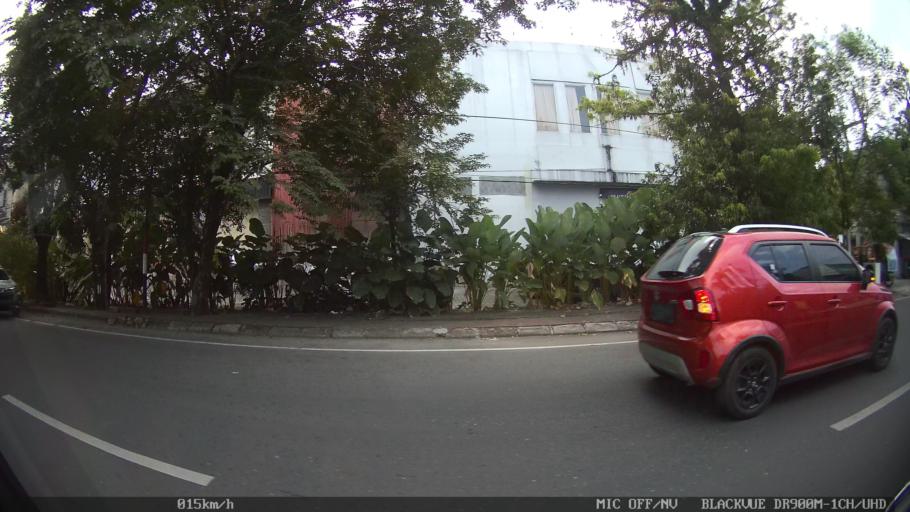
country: ID
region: North Sumatra
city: Medan
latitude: 3.5804
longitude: 98.6692
